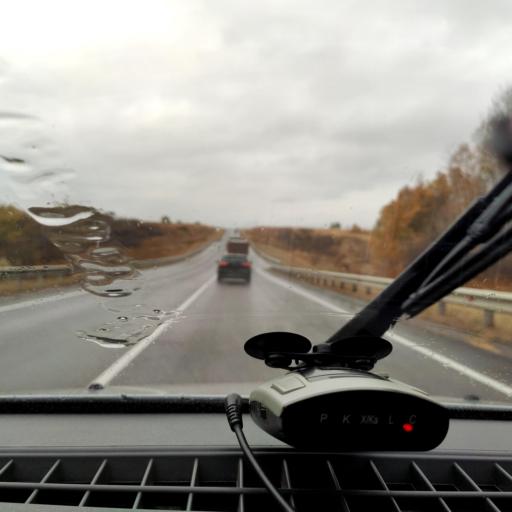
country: RU
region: Voronezj
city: Strelitsa
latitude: 51.5189
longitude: 38.9679
